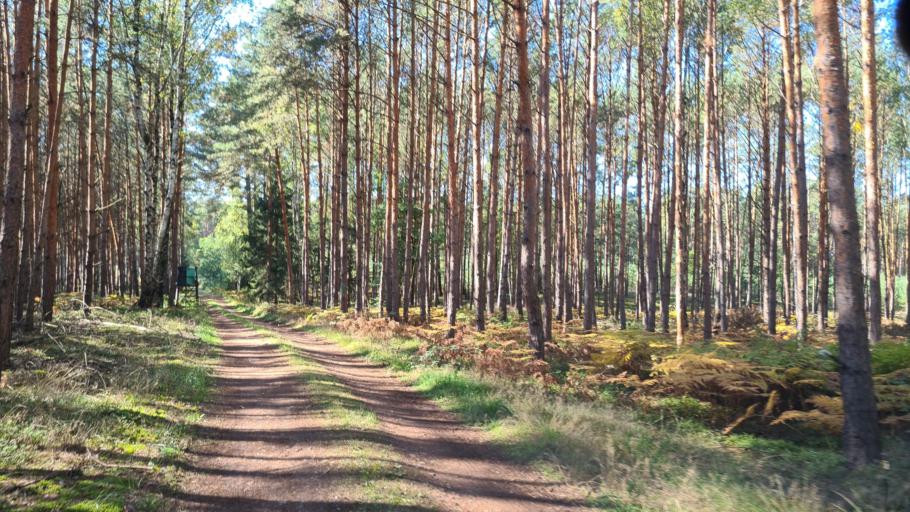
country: DE
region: Brandenburg
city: Lebusa
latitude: 51.8364
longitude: 13.4809
